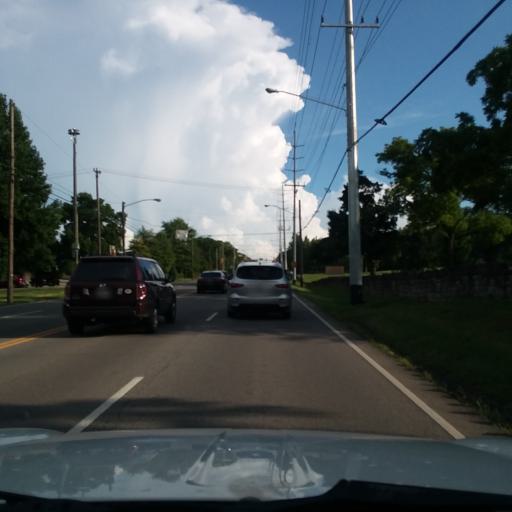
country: US
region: Tennessee
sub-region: Davidson County
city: Oak Hill
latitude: 36.0792
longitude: -86.7730
